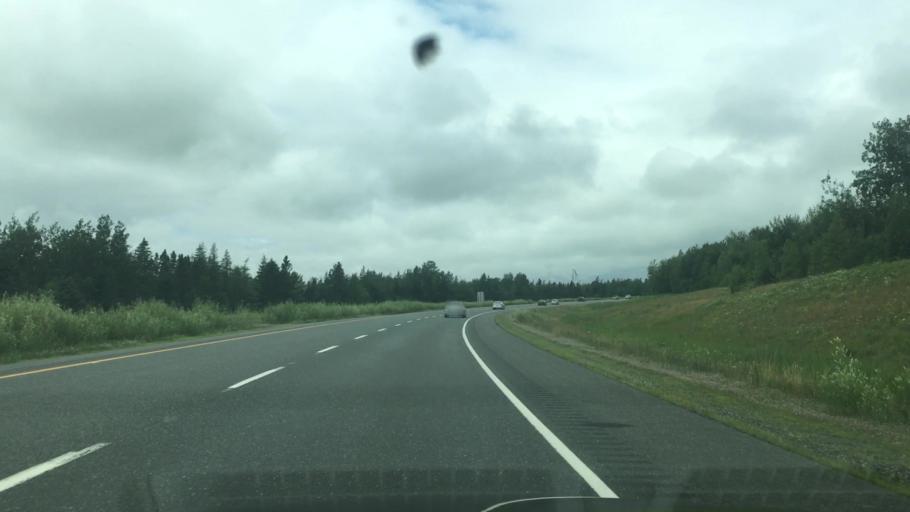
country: CA
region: Nova Scotia
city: Truro
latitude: 45.3817
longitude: -63.3547
